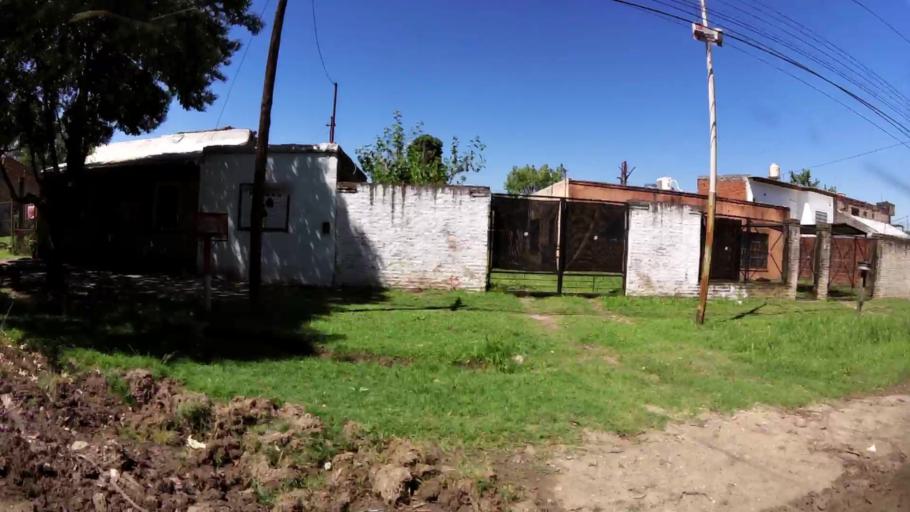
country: AR
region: Buenos Aires
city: Ituzaingo
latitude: -34.6736
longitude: -58.6596
